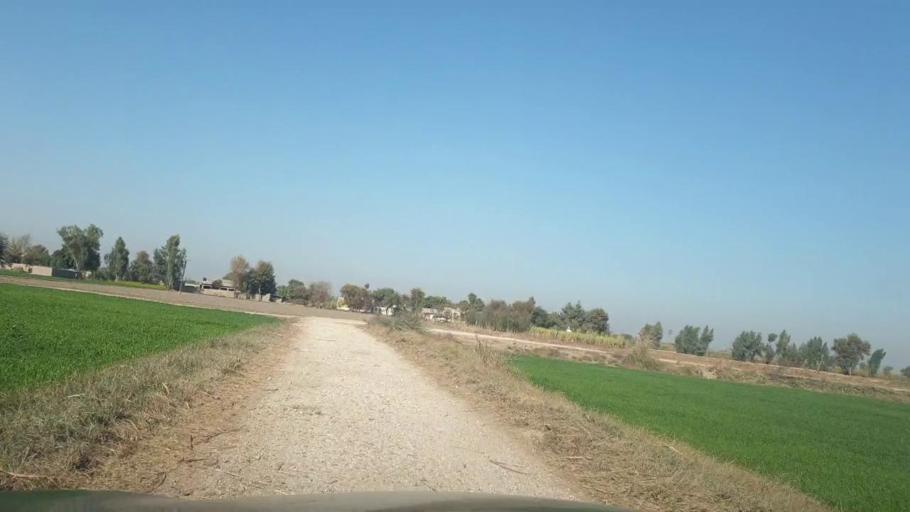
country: PK
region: Sindh
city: Mirpur Mathelo
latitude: 28.0078
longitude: 69.4786
